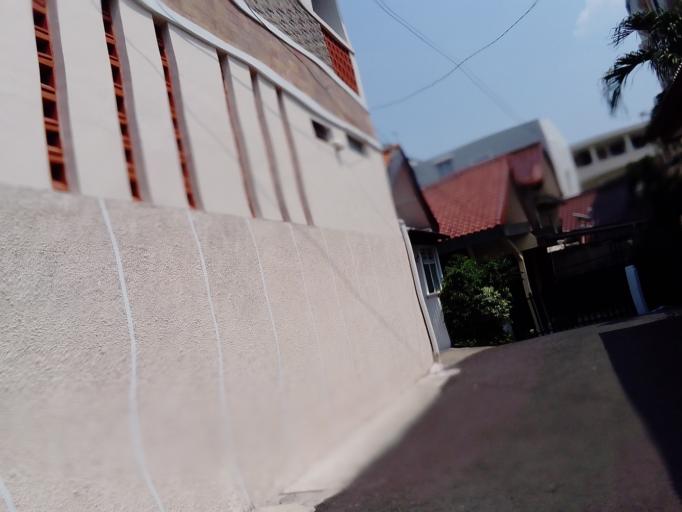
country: ID
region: Jakarta Raya
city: Jakarta
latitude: -6.2617
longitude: 106.7978
